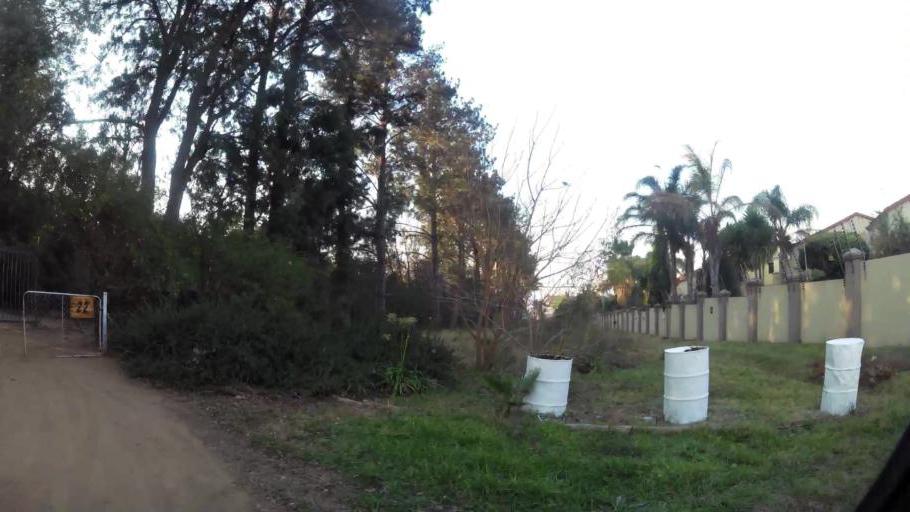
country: ZA
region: Gauteng
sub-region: City of Johannesburg Metropolitan Municipality
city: Diepsloot
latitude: -26.0037
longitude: 27.9912
